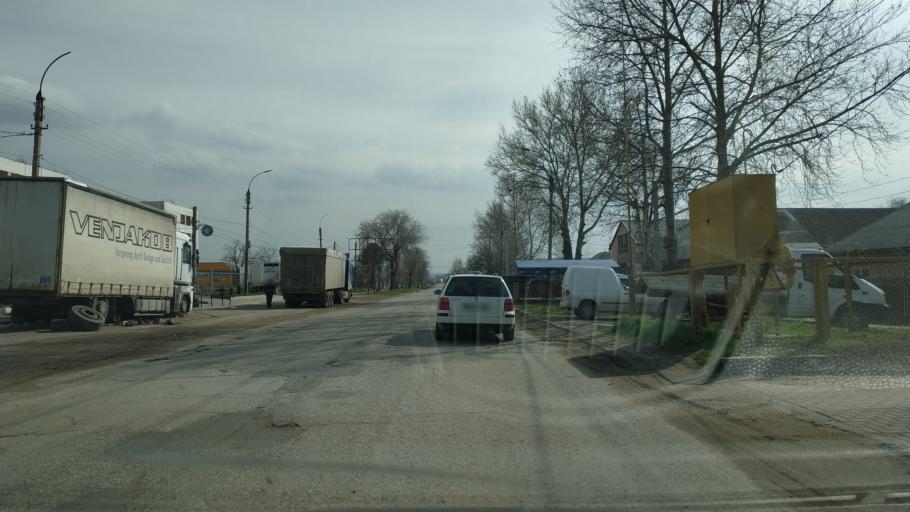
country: MD
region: Gagauzia
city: Vulcanesti
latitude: 45.6817
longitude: 28.4079
